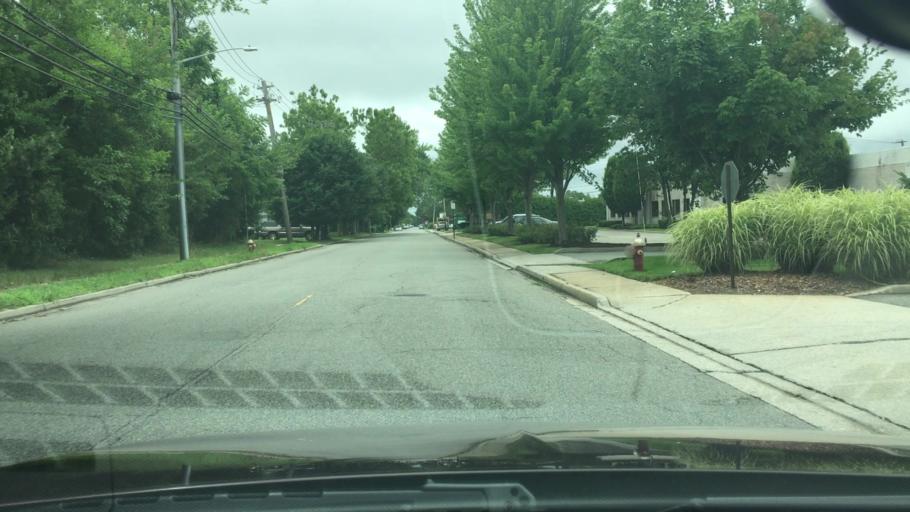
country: US
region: New York
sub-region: Nassau County
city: Hicksville
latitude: 40.7875
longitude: -73.5154
